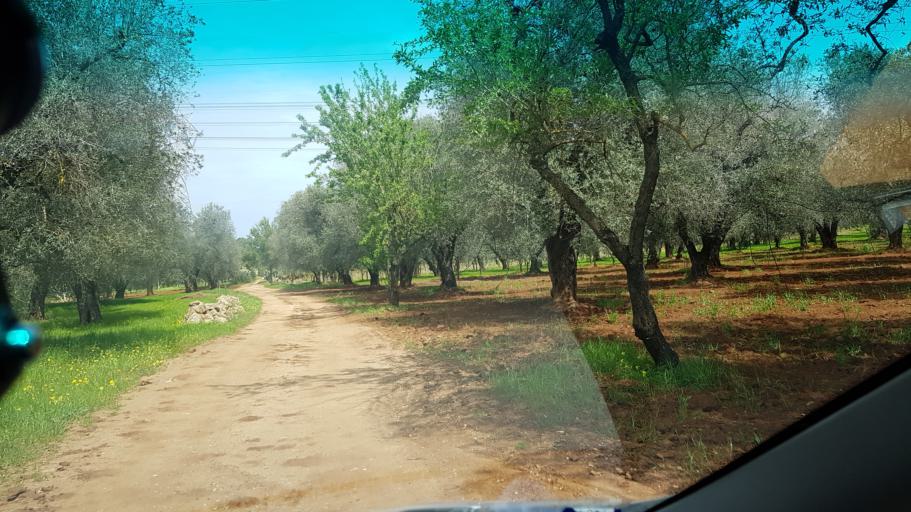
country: IT
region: Apulia
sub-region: Provincia di Brindisi
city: Mesagne
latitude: 40.6047
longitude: 17.8535
